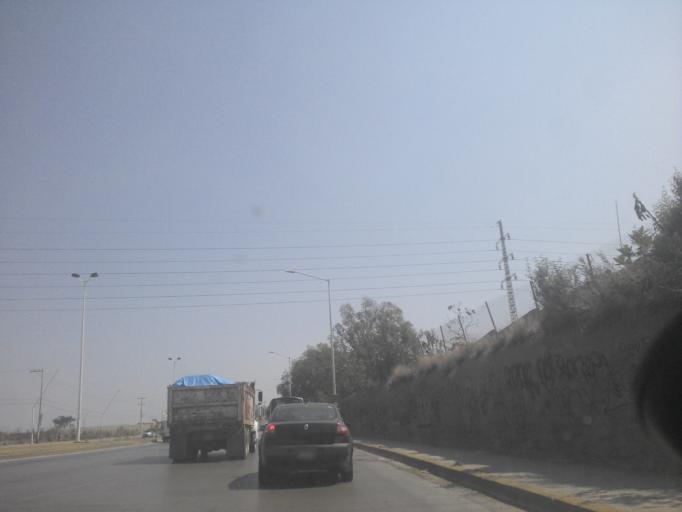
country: MX
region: Jalisco
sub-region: Tlajomulco de Zuniga
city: Altus Bosques
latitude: 20.5907
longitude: -103.3817
